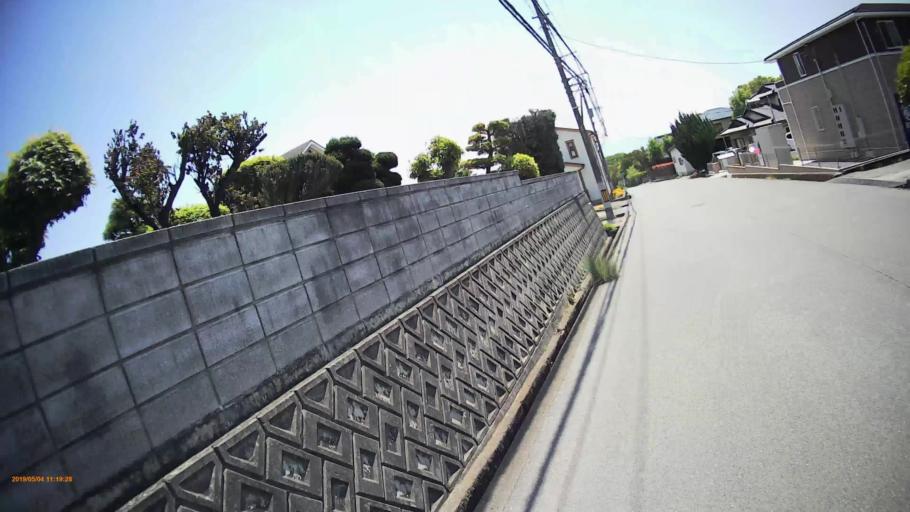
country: JP
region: Yamanashi
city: Nirasaki
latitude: 35.6934
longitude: 138.4742
